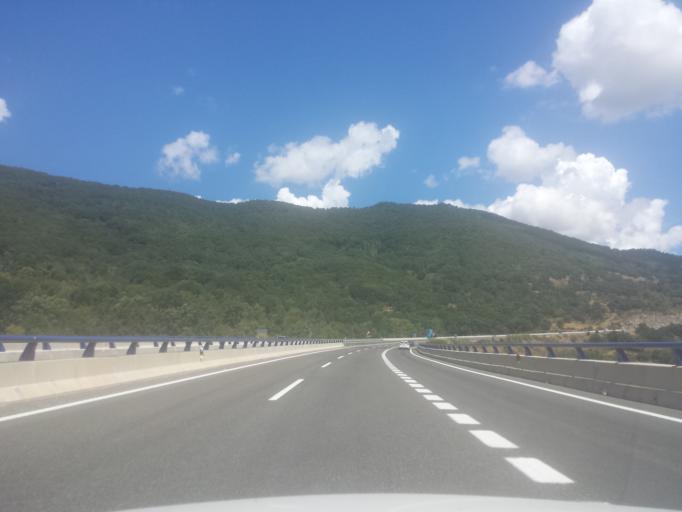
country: ES
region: Extremadura
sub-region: Provincia de Caceres
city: Banos de Montemayor
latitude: 40.3108
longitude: -5.8799
